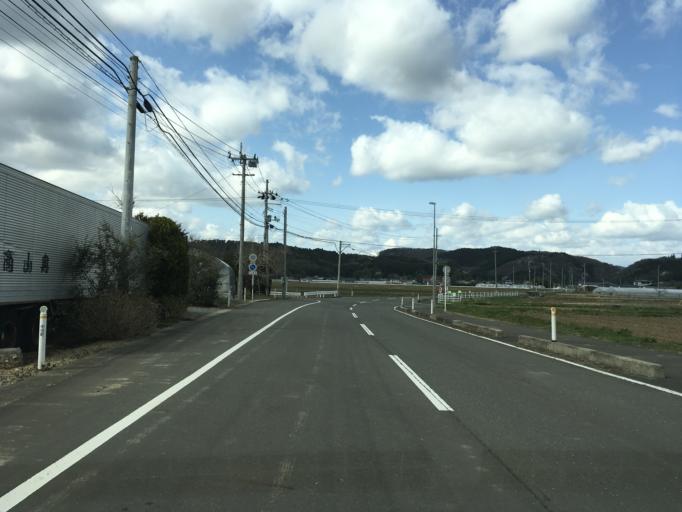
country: JP
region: Iwate
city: Ichinoseki
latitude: 38.7534
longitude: 141.2679
